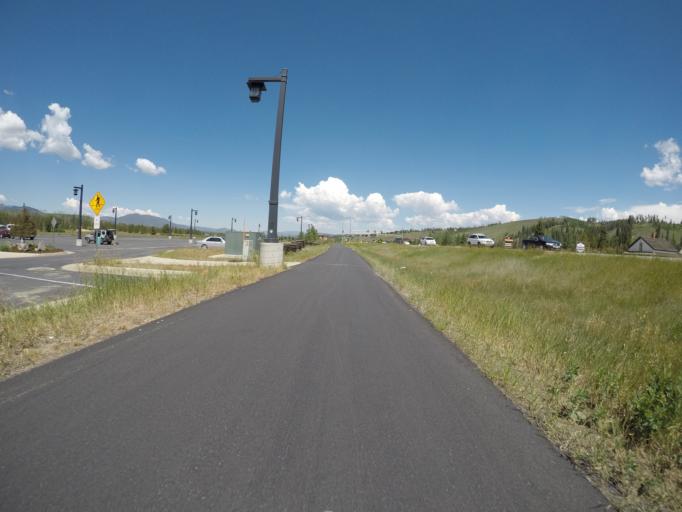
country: US
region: Colorado
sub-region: Grand County
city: Fraser
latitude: 39.9318
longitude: -105.7912
